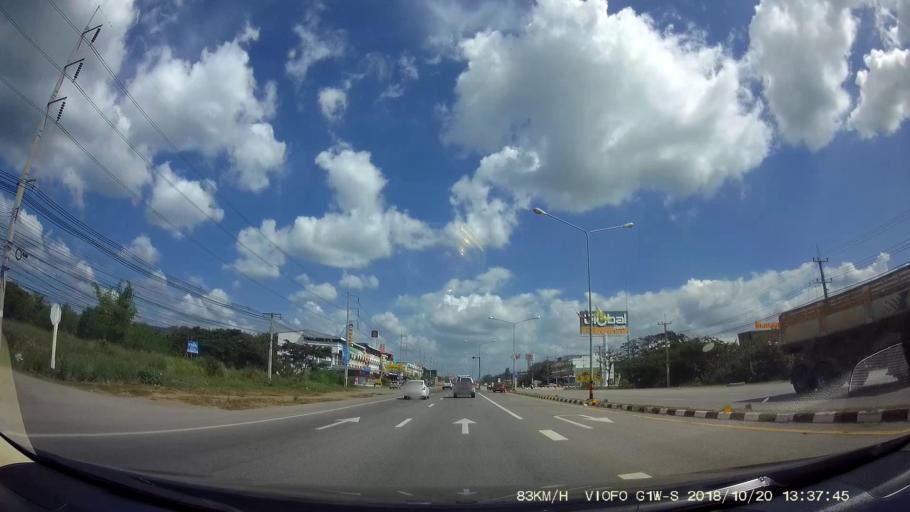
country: TH
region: Khon Kaen
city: Chum Phae
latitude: 16.5563
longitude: 102.0747
